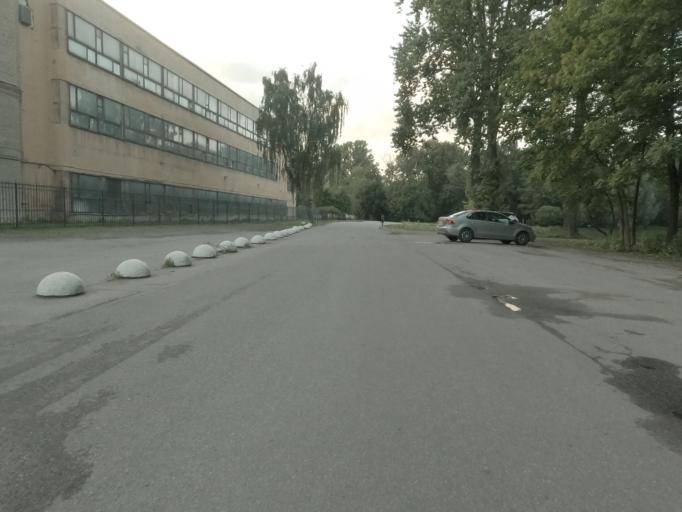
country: RU
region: St.-Petersburg
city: Admiralteisky
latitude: 59.8977
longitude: 30.2614
